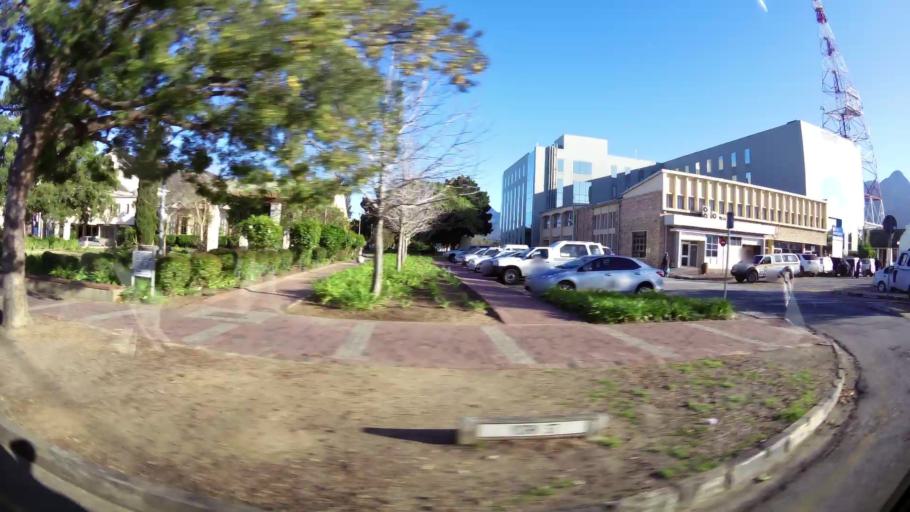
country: ZA
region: Western Cape
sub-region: Eden District Municipality
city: George
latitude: -33.9608
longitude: 22.4550
